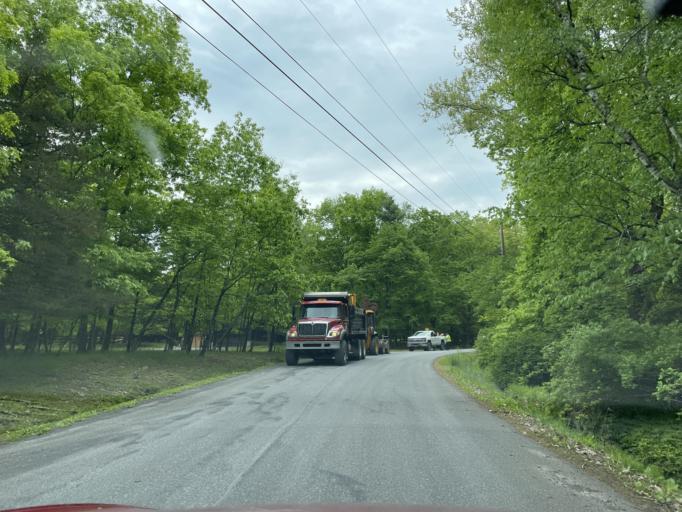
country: US
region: New York
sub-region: Ulster County
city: Woodstock
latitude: 42.0309
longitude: -74.1194
